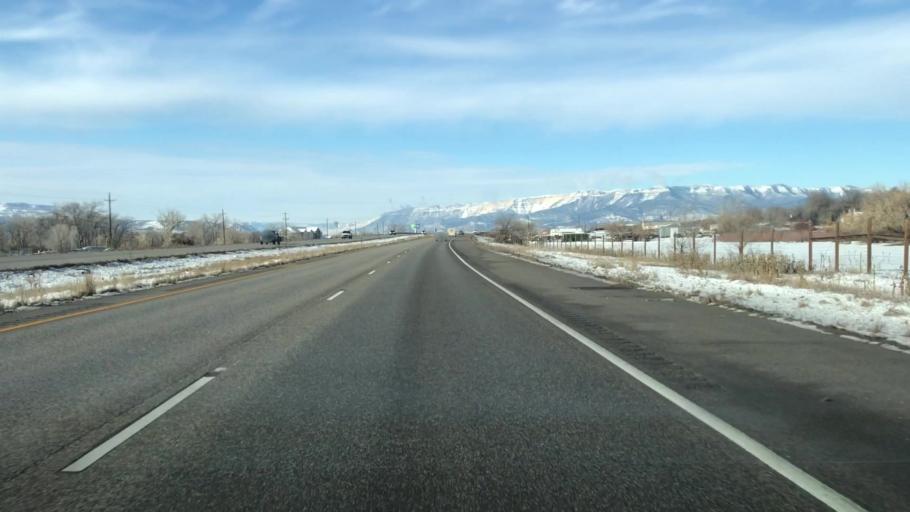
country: US
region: Colorado
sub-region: Garfield County
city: Silt
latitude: 39.5442
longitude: -107.6398
